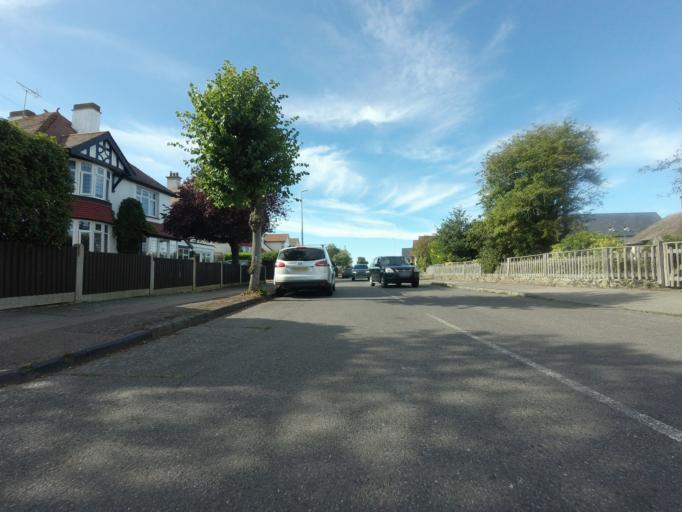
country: GB
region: England
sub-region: Kent
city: Herne Bay
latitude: 51.3707
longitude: 1.1474
